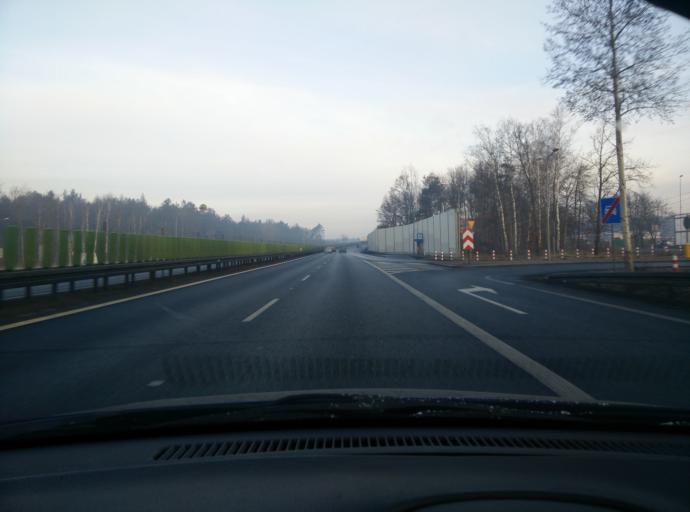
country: PL
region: Greater Poland Voivodeship
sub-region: Powiat poznanski
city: Kornik
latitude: 52.2959
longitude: 17.0520
